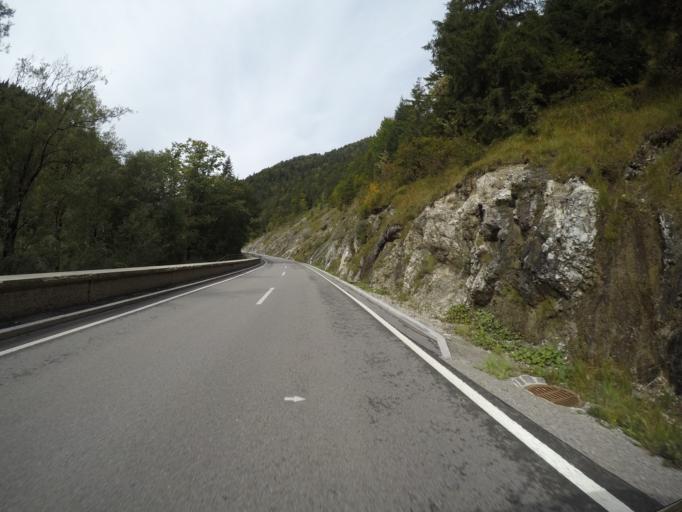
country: AT
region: Tyrol
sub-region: Politischer Bezirk Schwaz
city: Achenkirch
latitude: 47.5846
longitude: 11.6241
